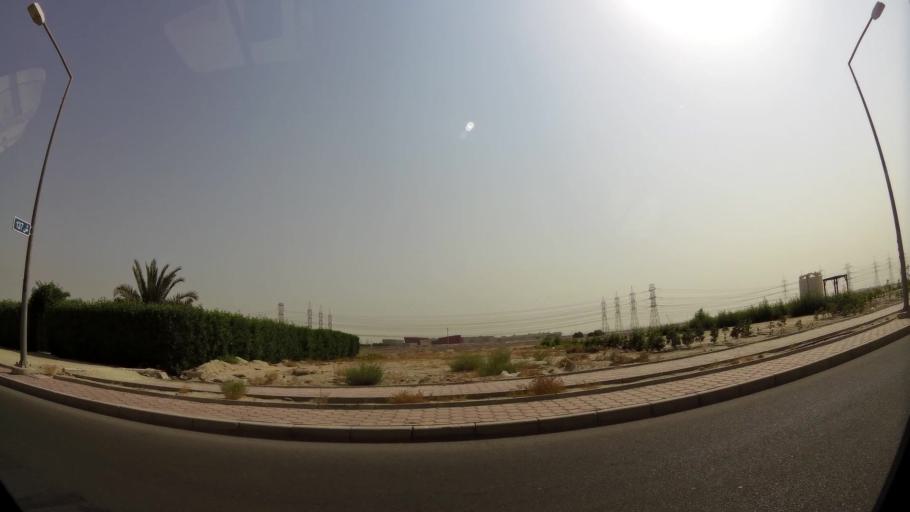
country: KW
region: Muhafazat al Jahra'
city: Al Jahra'
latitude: 29.3256
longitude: 47.7791
